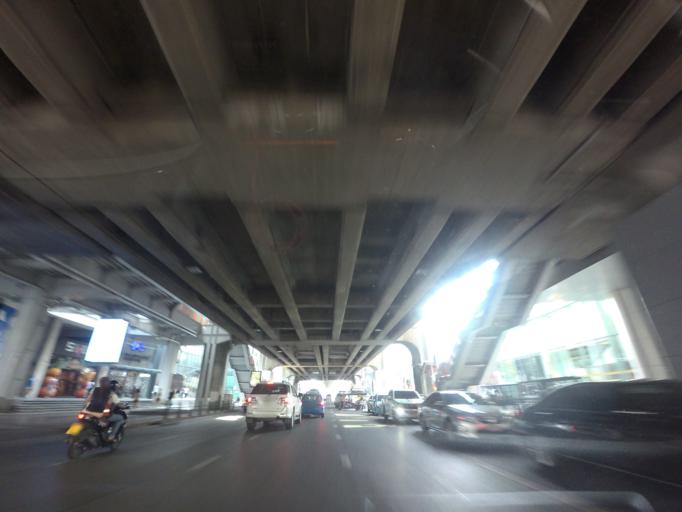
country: TH
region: Bangkok
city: Ratchathewi
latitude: 13.7459
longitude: 100.5345
